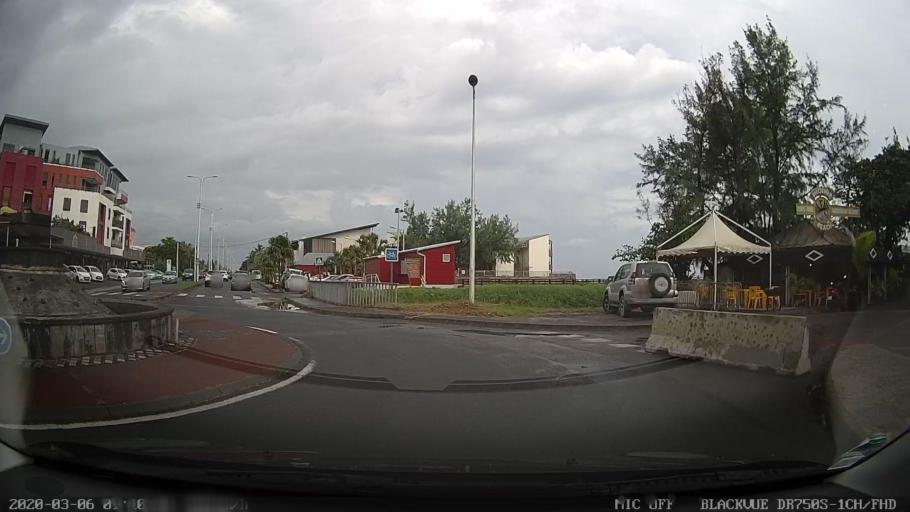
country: RE
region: Reunion
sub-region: Reunion
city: Saint-Pierre
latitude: -21.3412
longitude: 55.4610
